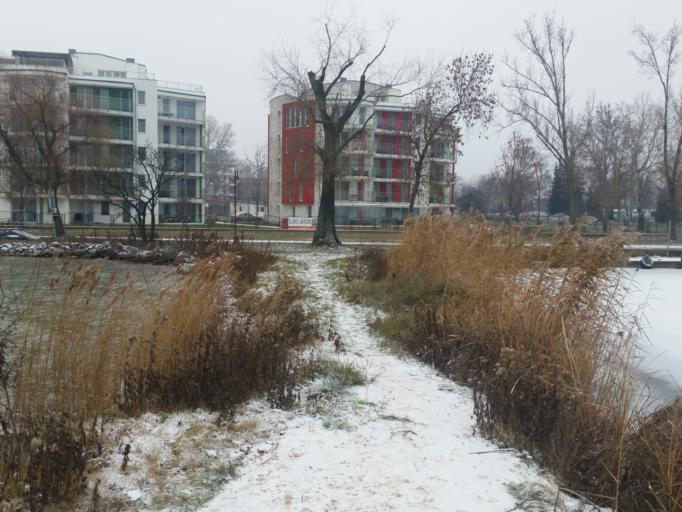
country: HU
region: Somogy
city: Siofok
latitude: 46.9033
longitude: 18.0174
